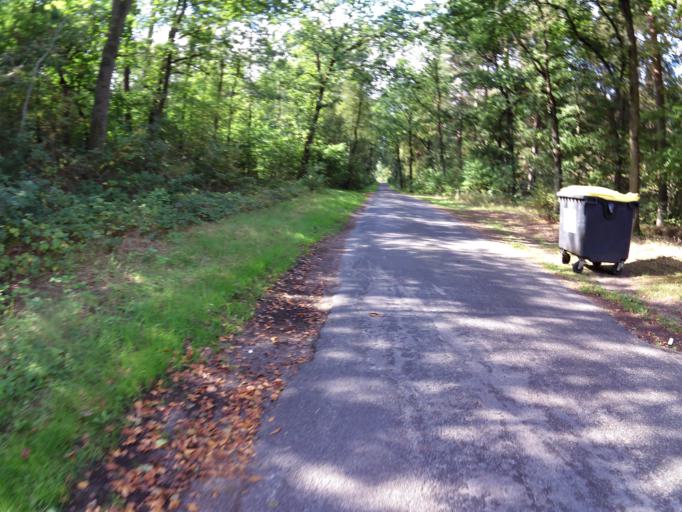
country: DE
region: Lower Saxony
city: Bremervorde
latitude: 53.4691
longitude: 9.1433
